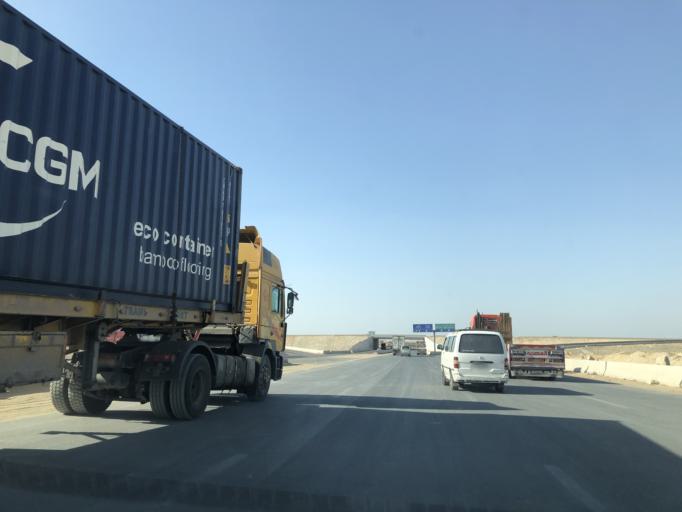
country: EG
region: Muhafazat al Minufiyah
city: Ashmun
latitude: 30.0642
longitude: 30.8459
